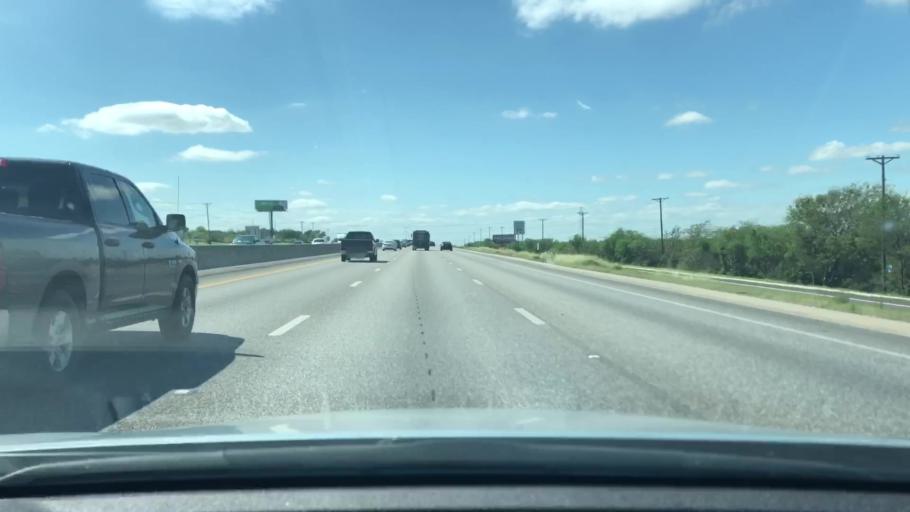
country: US
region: Texas
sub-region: Guadalupe County
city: Northcliff
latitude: 29.6469
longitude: -98.2007
